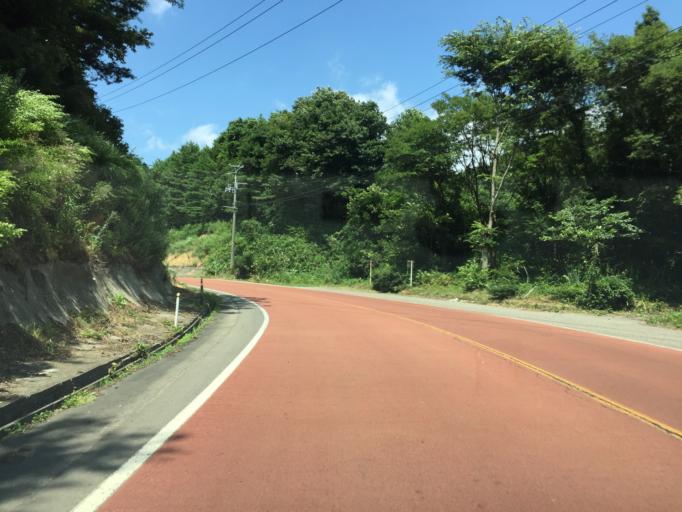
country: JP
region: Fukushima
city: Inawashiro
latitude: 37.5052
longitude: 139.9954
